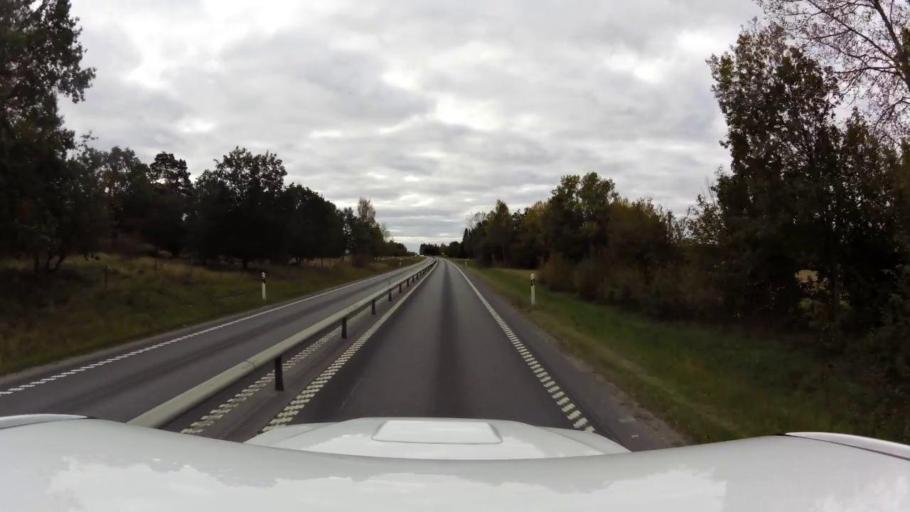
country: SE
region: OEstergoetland
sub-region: Linkopings Kommun
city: Malmslatt
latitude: 58.3643
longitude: 15.5445
